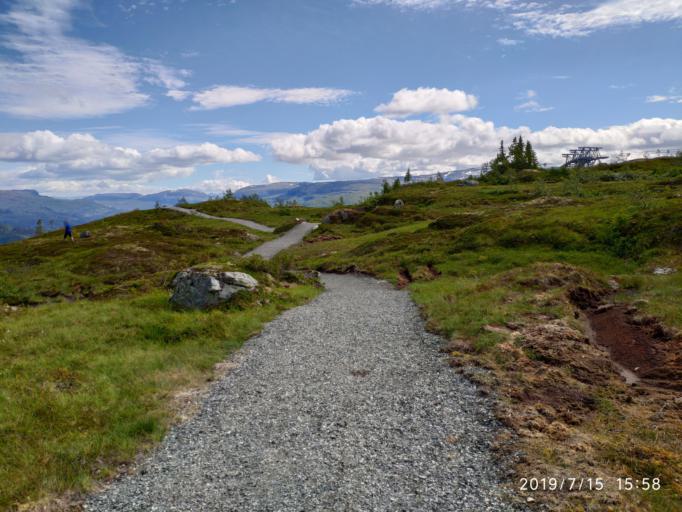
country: NO
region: Hordaland
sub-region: Voss
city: Voss
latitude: 60.6455
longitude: 6.4060
